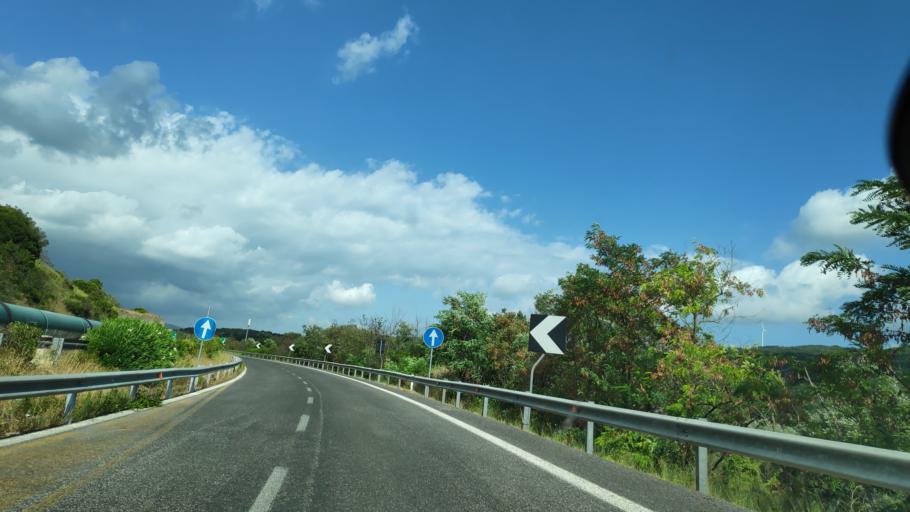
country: IT
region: Campania
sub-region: Provincia di Salerno
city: Serre
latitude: 40.6156
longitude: 15.1771
